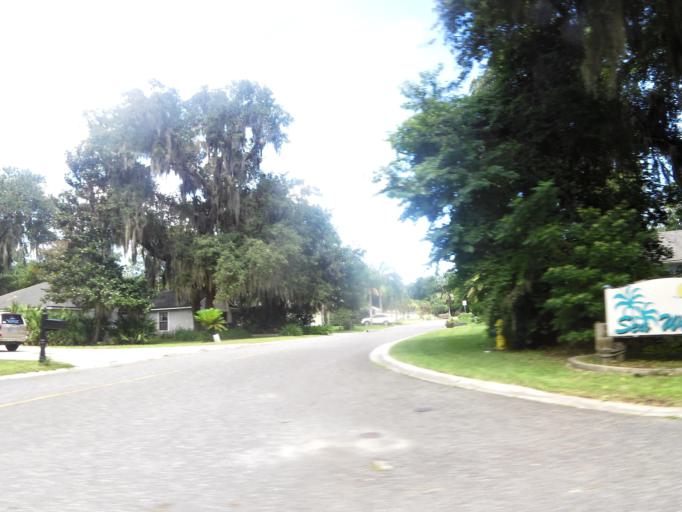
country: US
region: Florida
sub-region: Nassau County
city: Fernandina Beach
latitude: 30.6357
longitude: -81.4623
